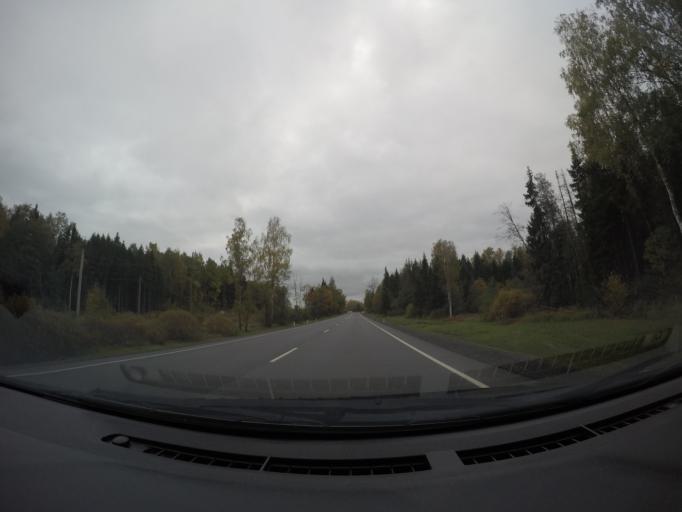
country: RU
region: Moskovskaya
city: Ruza
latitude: 55.7194
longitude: 36.2119
